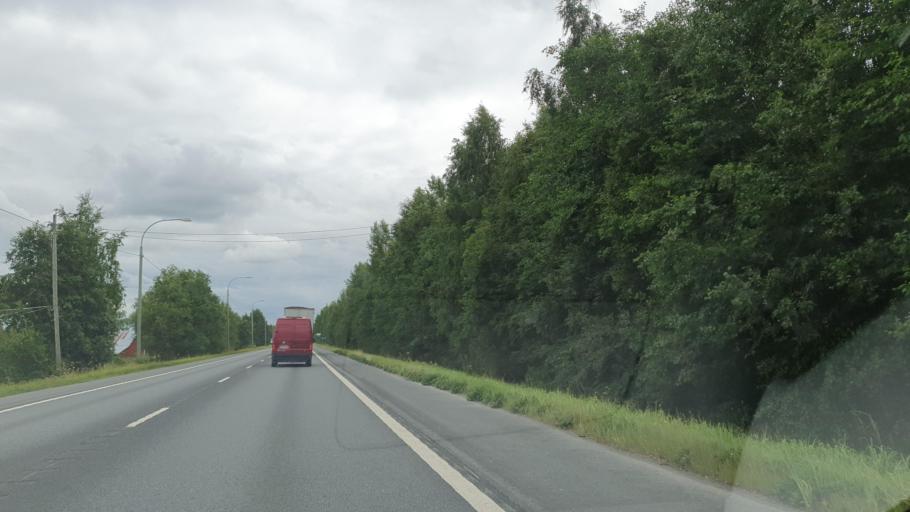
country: FI
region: Northern Savo
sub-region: Ylae-Savo
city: Iisalmi
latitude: 63.5029
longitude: 27.2618
